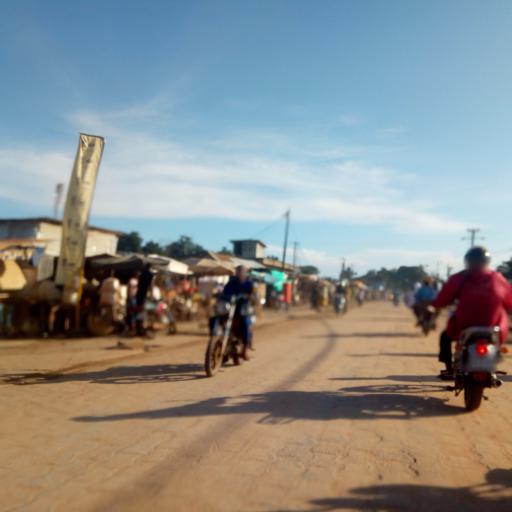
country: BJ
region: Atlantique
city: Hevie
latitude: 6.3896
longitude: 2.2722
